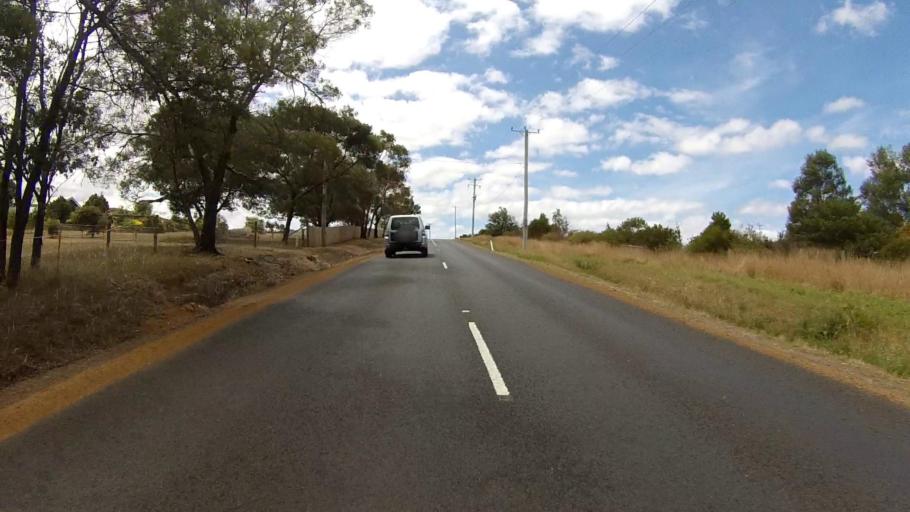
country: AU
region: Tasmania
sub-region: Sorell
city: Sorell
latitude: -42.8156
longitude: 147.6131
